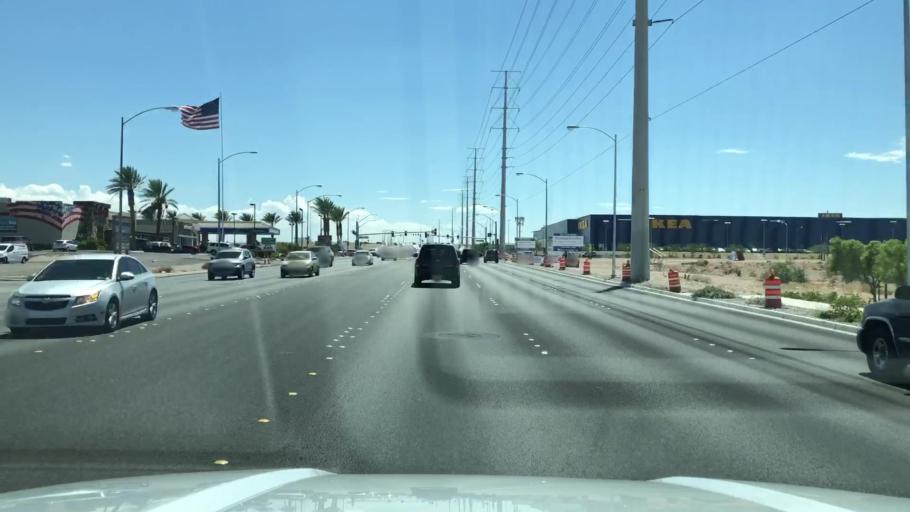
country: US
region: Nevada
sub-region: Clark County
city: Spring Valley
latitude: 36.0724
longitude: -115.2795
